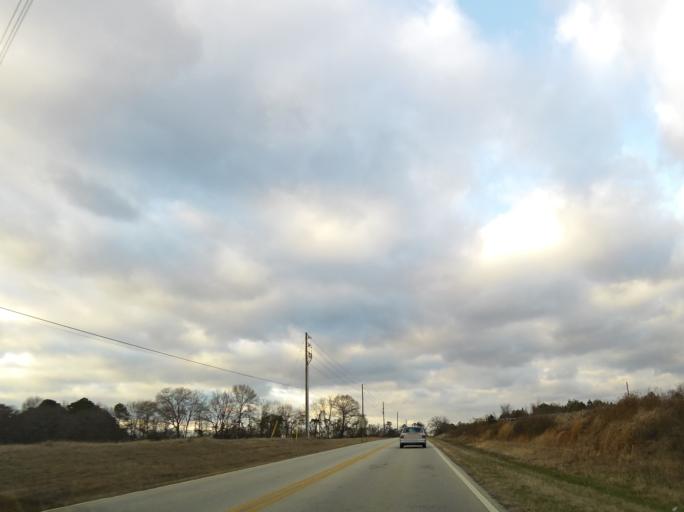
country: US
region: Georgia
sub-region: Houston County
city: Robins Air Force Base
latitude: 32.5584
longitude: -83.5862
